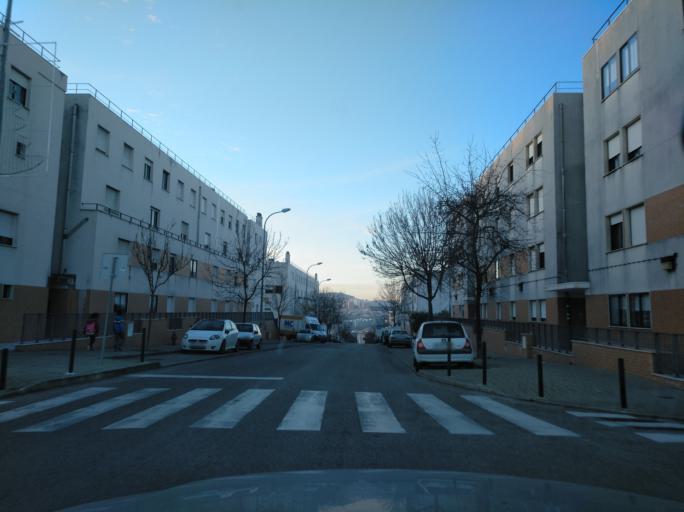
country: PT
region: Lisbon
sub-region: Odivelas
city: Olival do Basto
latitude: 38.7915
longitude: -9.1524
